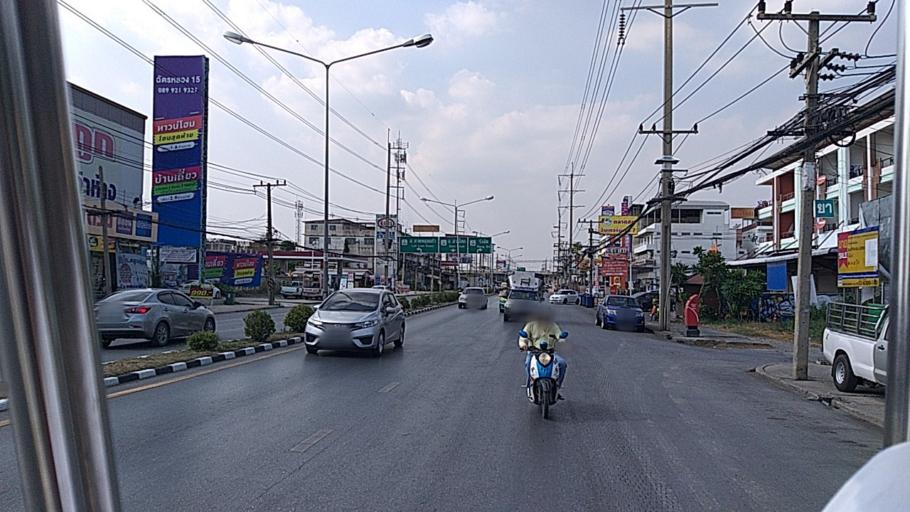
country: TH
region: Pathum Thani
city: Pathum Thani
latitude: 14.0267
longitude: 100.5254
